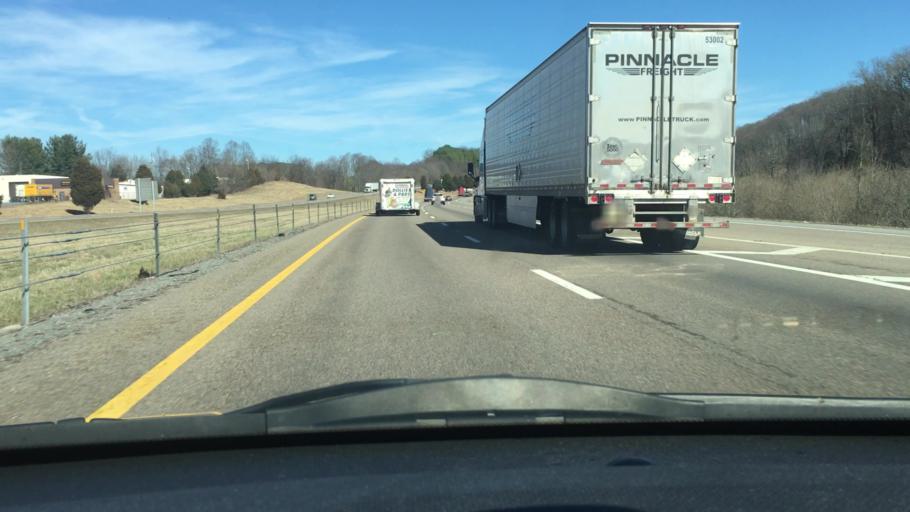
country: US
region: Tennessee
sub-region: Sullivan County
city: Blountville
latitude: 36.5354
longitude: -82.3842
